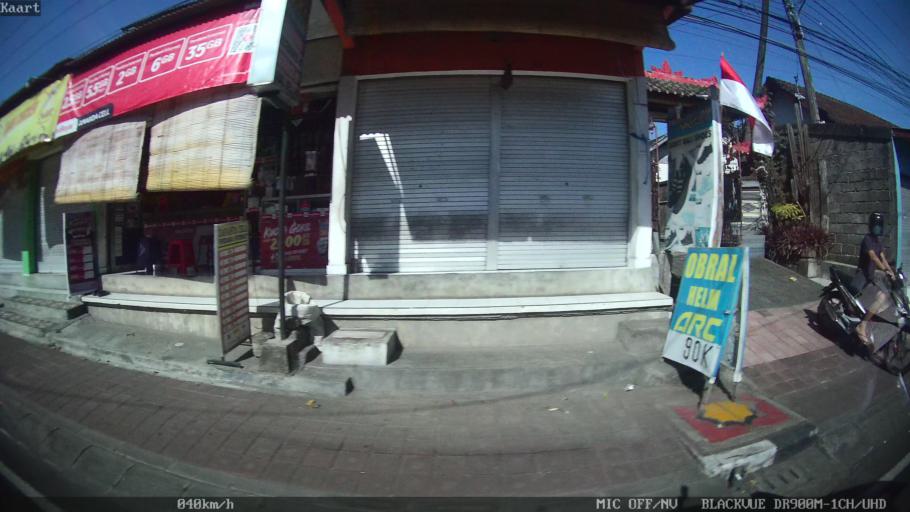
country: ID
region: Bali
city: Banjar Gunungpande
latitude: -8.6256
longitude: 115.1745
